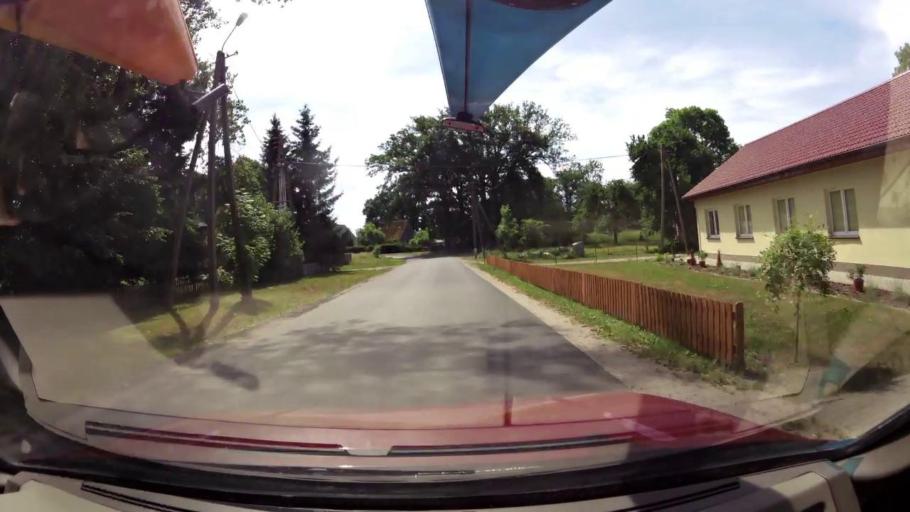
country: PL
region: West Pomeranian Voivodeship
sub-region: Powiat slawienski
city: Darlowo
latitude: 54.3057
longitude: 16.4795
